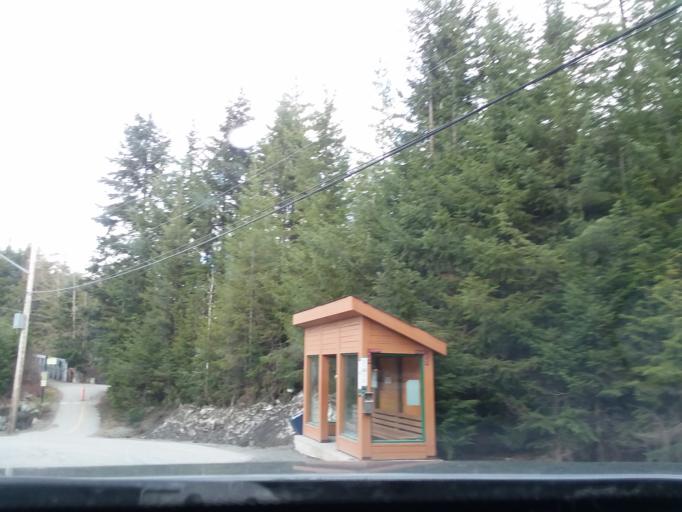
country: CA
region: British Columbia
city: Whistler
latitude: 50.1027
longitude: -122.9819
